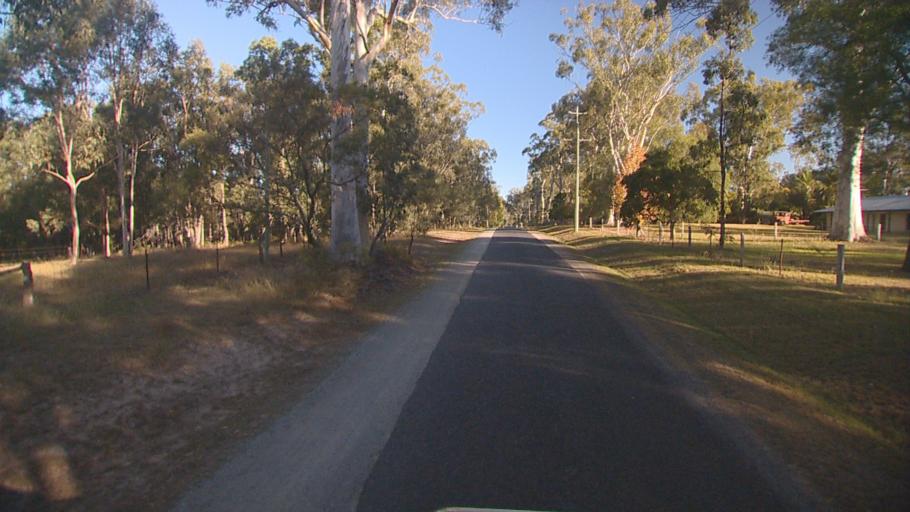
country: AU
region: Queensland
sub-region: Logan
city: Chambers Flat
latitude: -27.7865
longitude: 153.0862
